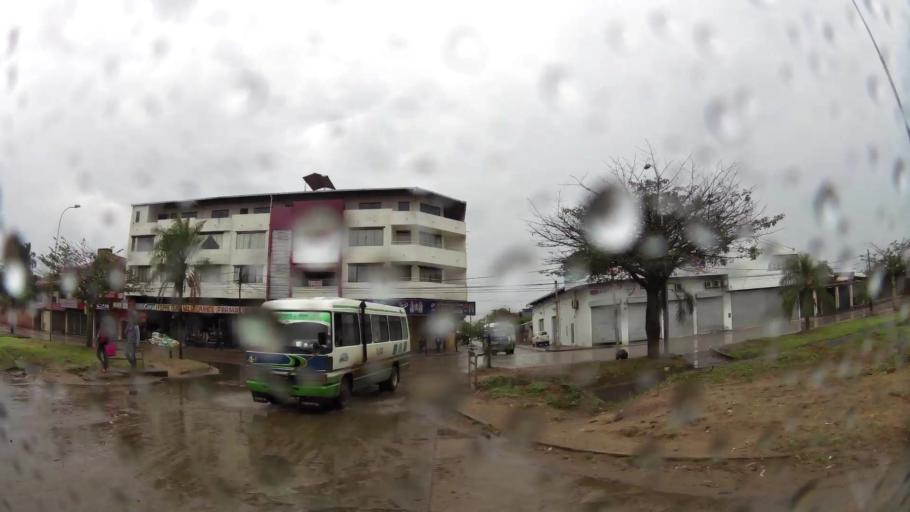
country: BO
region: Santa Cruz
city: Santa Cruz de la Sierra
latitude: -17.8146
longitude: -63.2227
